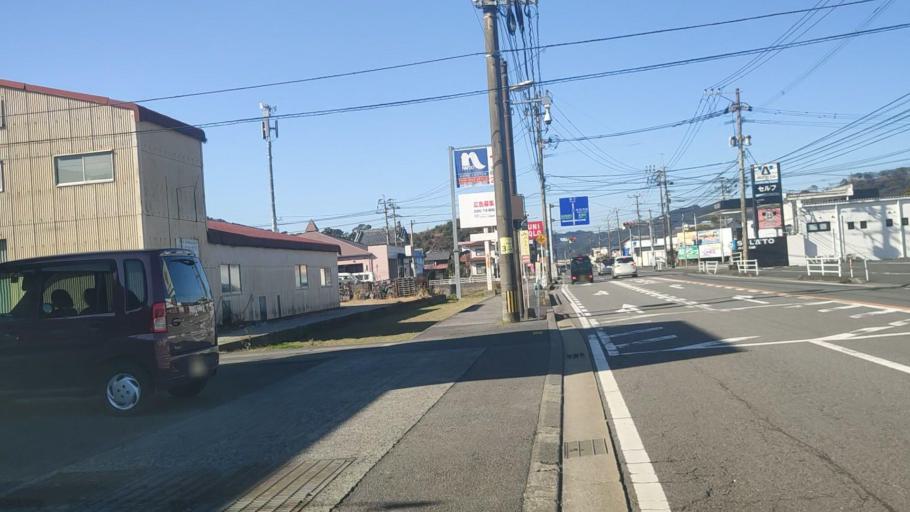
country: JP
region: Oita
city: Saiki
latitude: 32.9457
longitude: 131.9023
